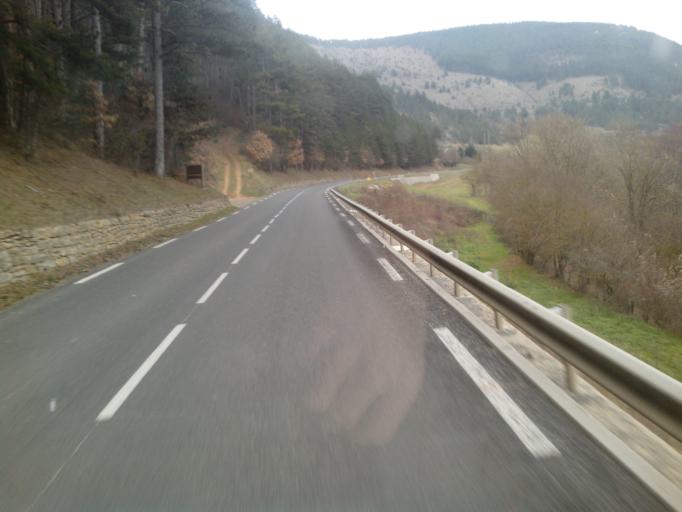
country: FR
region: Languedoc-Roussillon
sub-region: Departement de la Lozere
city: Mende
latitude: 44.4733
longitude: 3.4753
